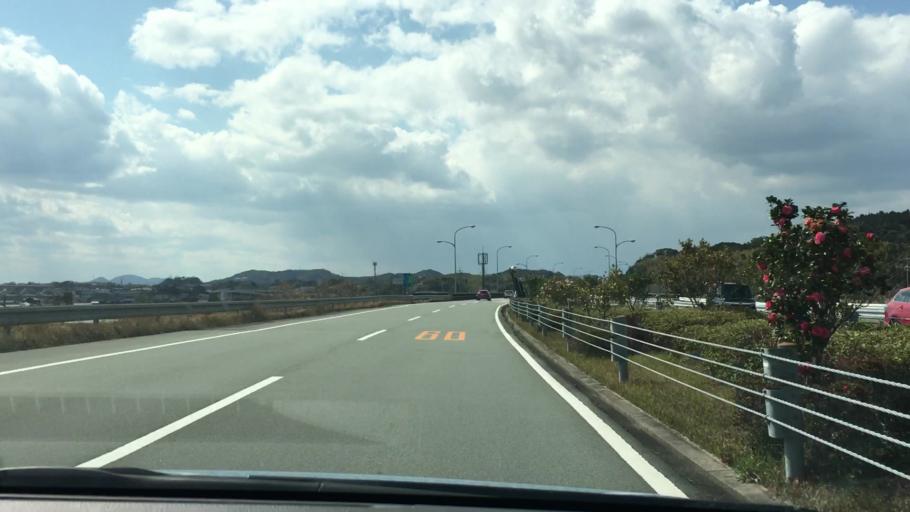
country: JP
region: Mie
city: Ise
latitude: 34.4790
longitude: 136.7419
